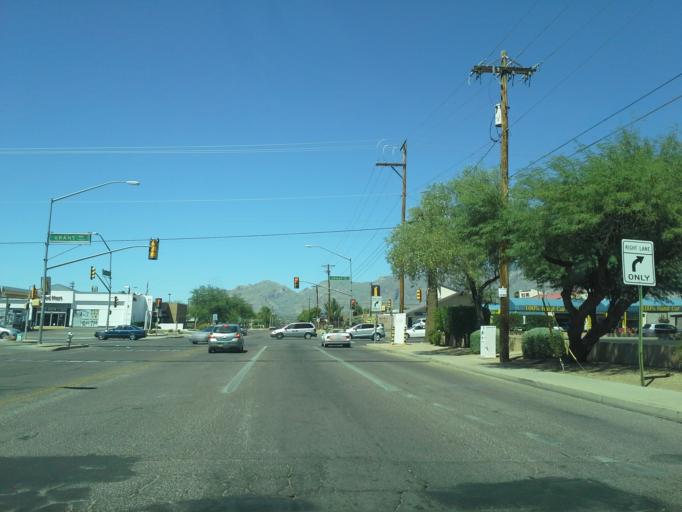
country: US
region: Arizona
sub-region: Pima County
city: Tucson
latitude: 32.2498
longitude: -110.9354
